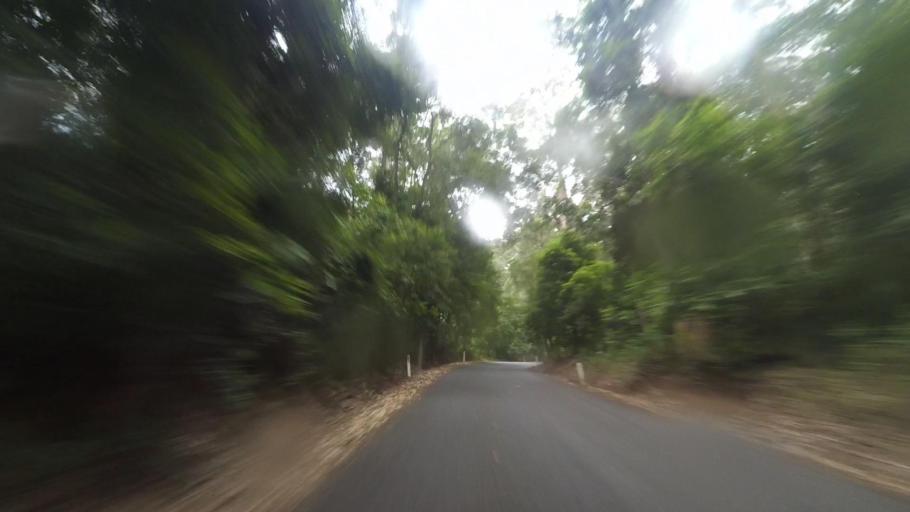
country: AU
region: New South Wales
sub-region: Wollongong
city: Mount Keira
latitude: -34.4031
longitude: 150.8229
